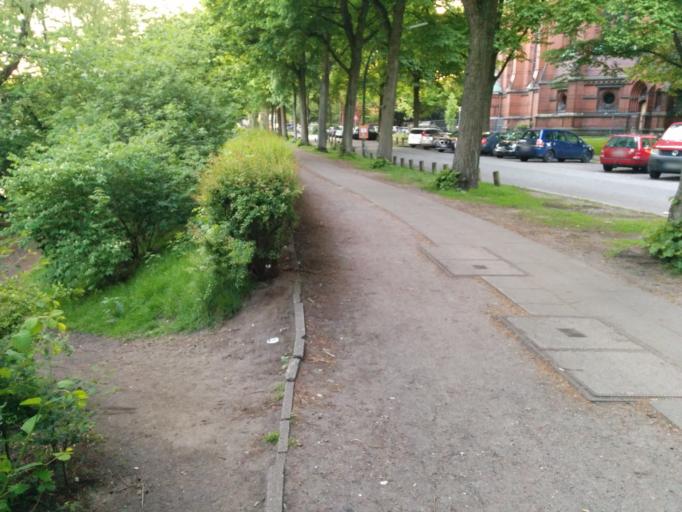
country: DE
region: Hamburg
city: Borgfelde
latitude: 53.5671
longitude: 10.0290
